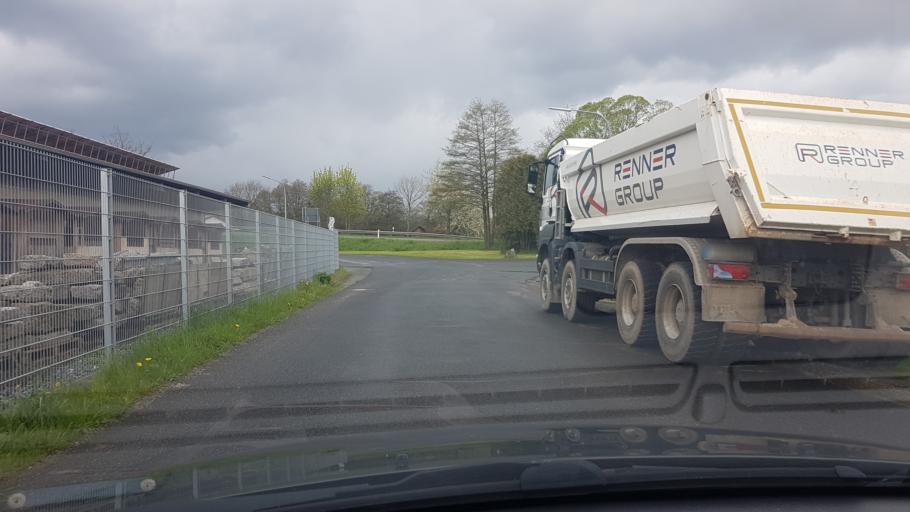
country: DE
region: Bavaria
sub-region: Upper Palatinate
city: Erbendorf
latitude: 49.8348
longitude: 12.0642
